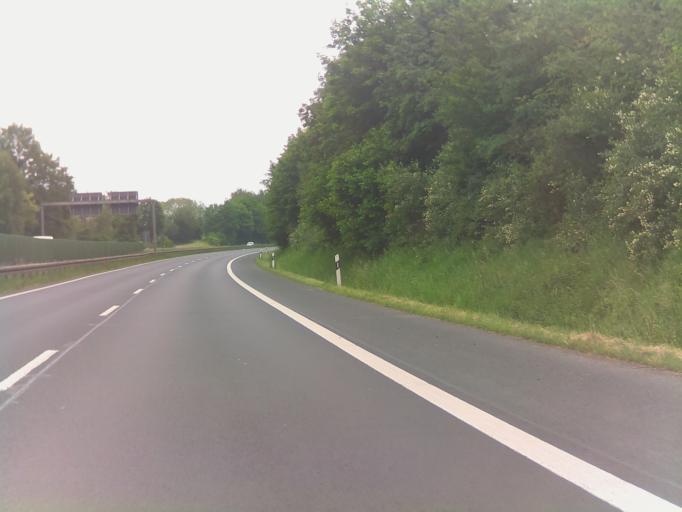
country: DE
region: Hesse
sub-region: Regierungsbezirk Kassel
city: Eichenzell
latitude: 50.5158
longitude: 9.6847
